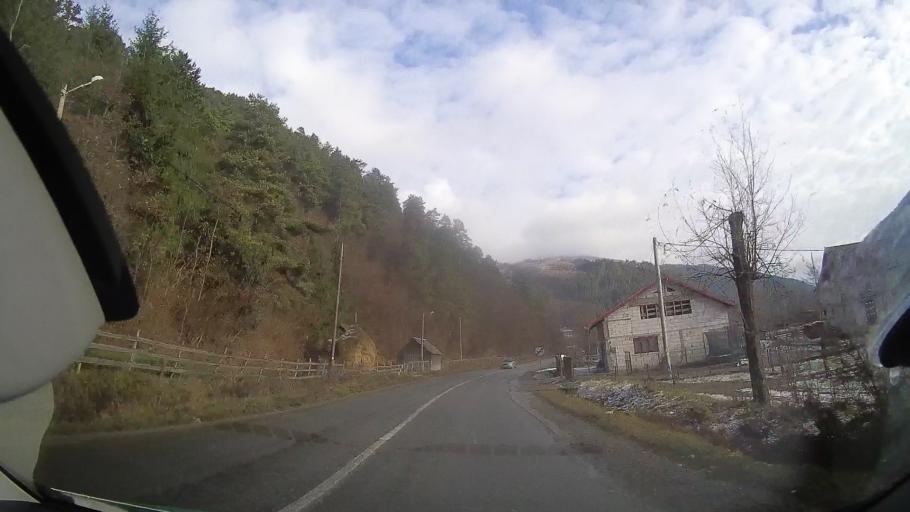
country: RO
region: Alba
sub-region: Comuna Bistra
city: Bistra
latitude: 46.3808
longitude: 23.1214
